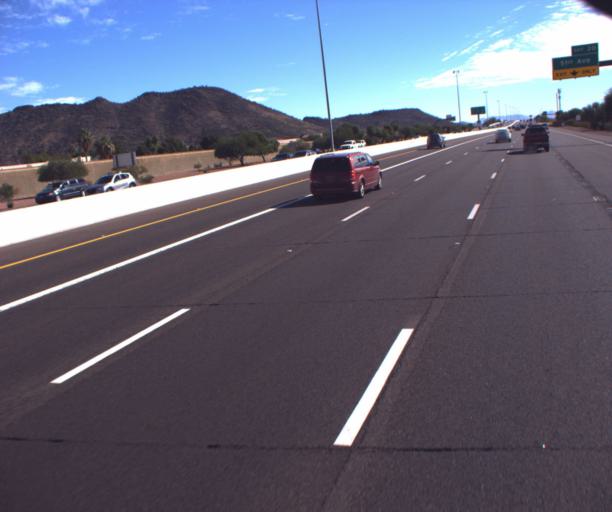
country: US
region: Arizona
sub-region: Maricopa County
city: Peoria
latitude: 33.6682
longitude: -112.1806
